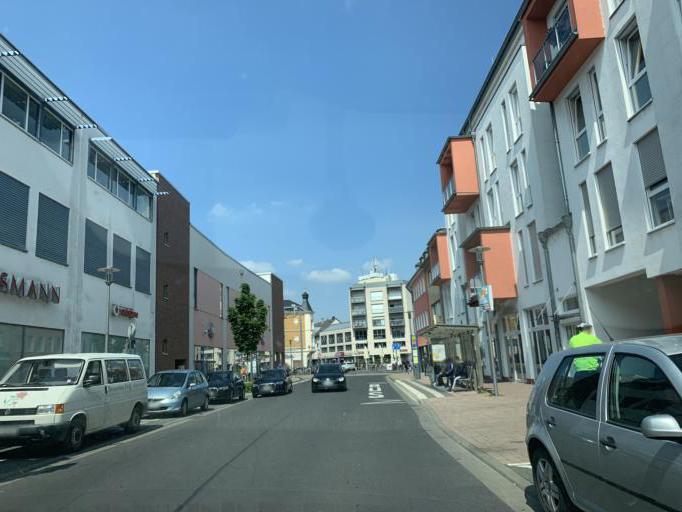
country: DE
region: North Rhine-Westphalia
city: Bruhl
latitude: 50.8256
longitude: 6.9009
